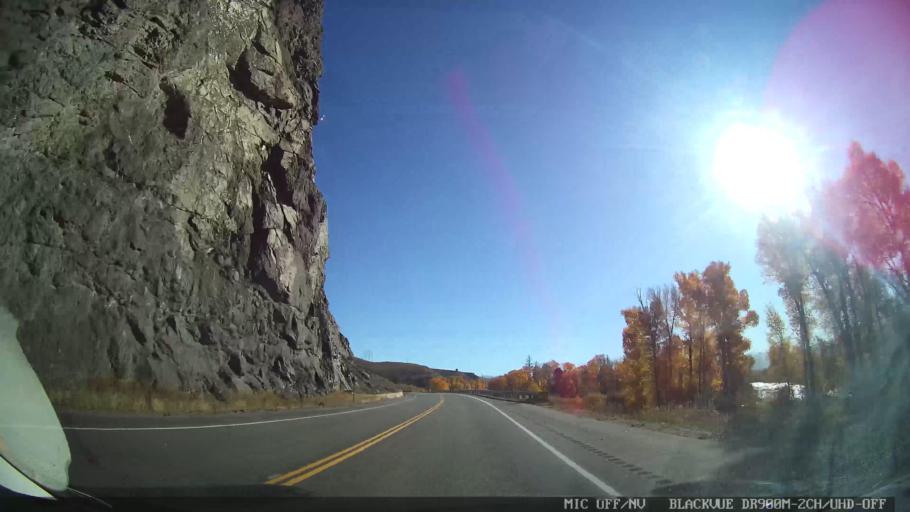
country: US
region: Colorado
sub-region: Grand County
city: Granby
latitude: 40.1093
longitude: -106.0014
